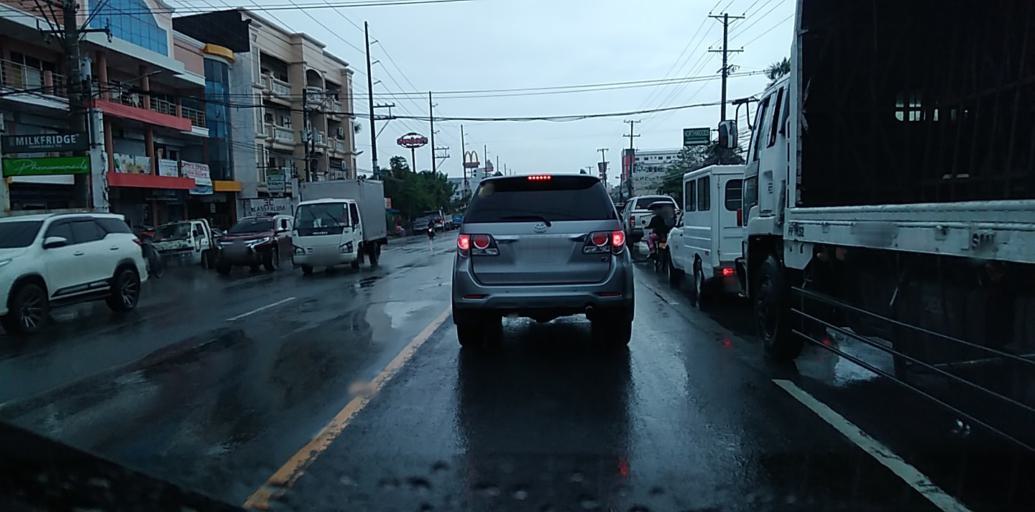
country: PH
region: Central Luzon
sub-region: Province of Pampanga
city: Bulaon
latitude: 15.0669
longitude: 120.6502
